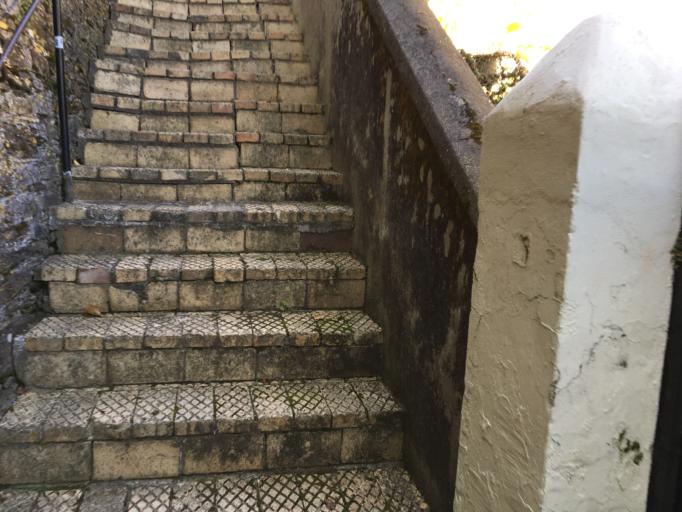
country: GB
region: England
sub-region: Devon
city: Dartmouth
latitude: 50.3474
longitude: -3.5777
